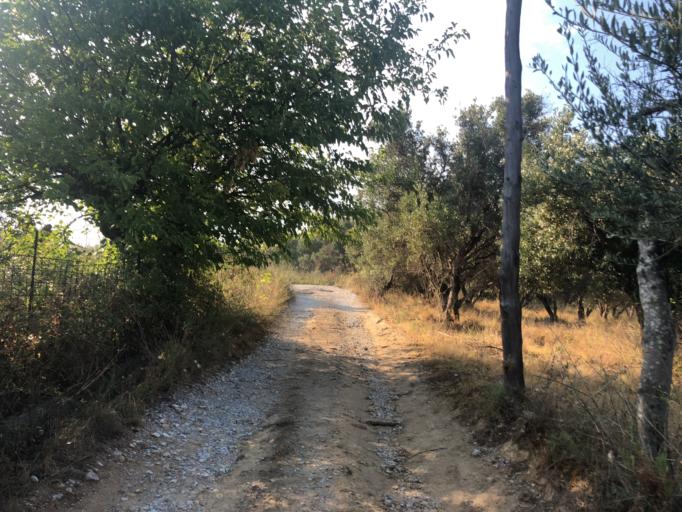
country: GR
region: Crete
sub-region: Nomos Chanias
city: Georgioupolis
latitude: 35.3466
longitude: 24.3070
